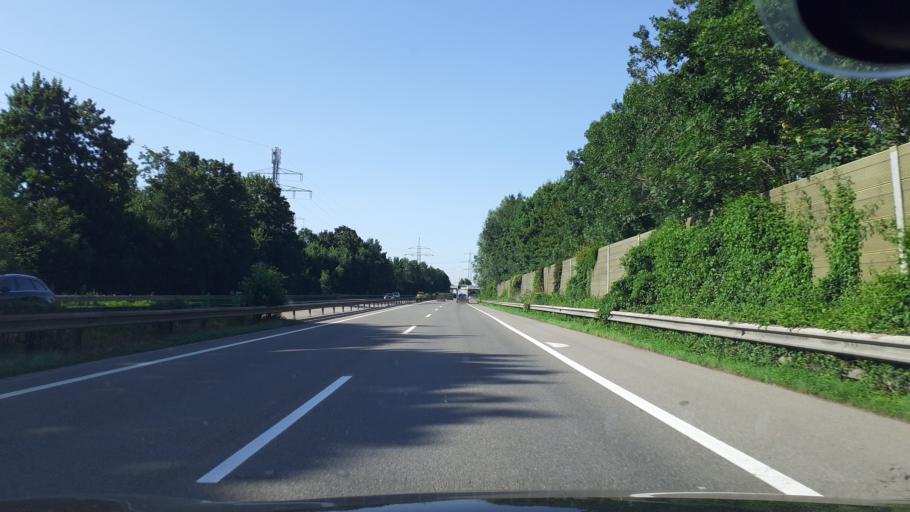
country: AT
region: Vorarlberg
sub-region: Politischer Bezirk Feldkirch
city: Altach
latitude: 47.3487
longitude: 9.6358
